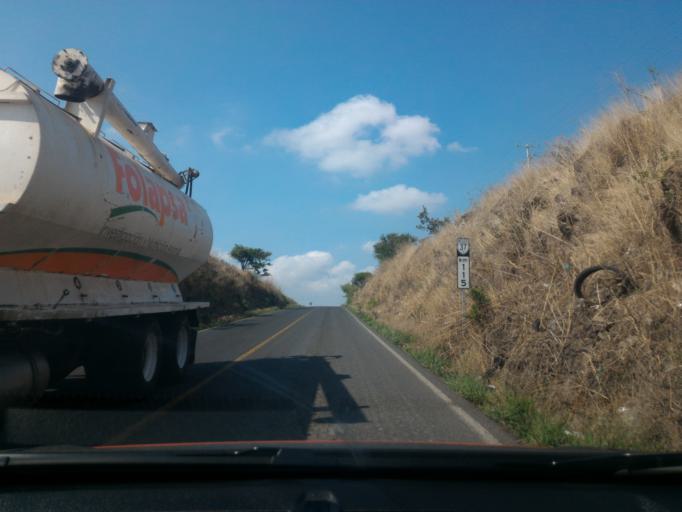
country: MX
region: Guanajuato
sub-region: Penjamo
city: Estacion la Piedad
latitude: 20.4319
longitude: -101.9899
